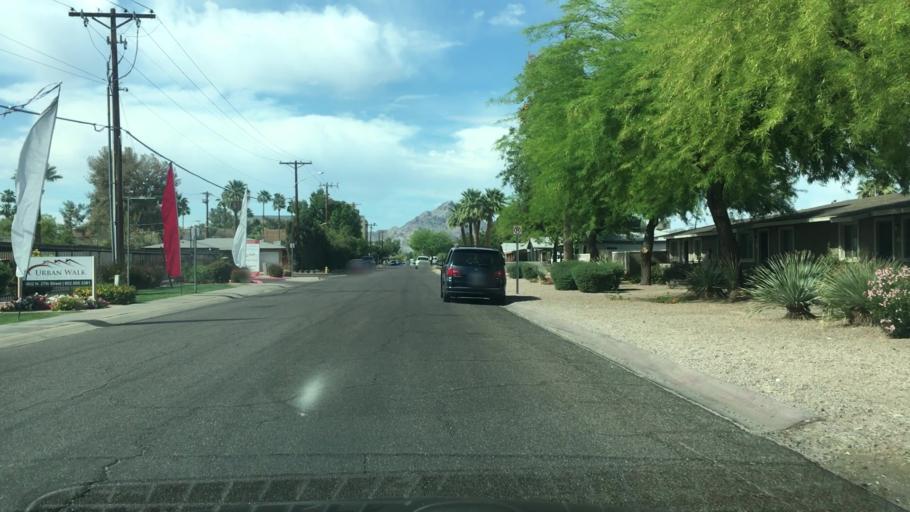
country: US
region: Arizona
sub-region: Maricopa County
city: Phoenix
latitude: 33.4916
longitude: -112.0238
